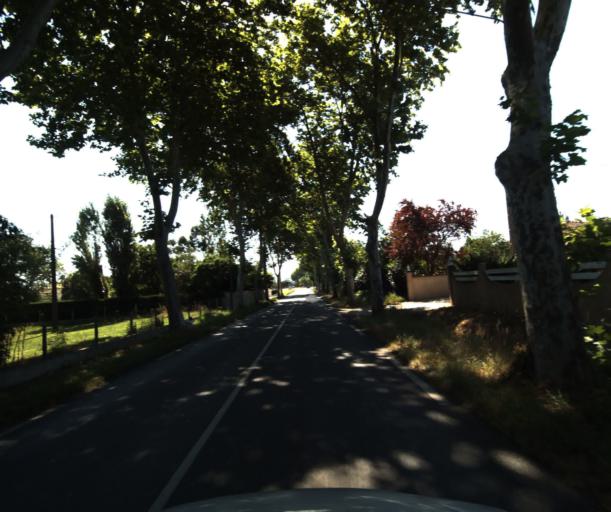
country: FR
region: Midi-Pyrenees
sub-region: Departement de la Haute-Garonne
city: Eaunes
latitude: 43.4213
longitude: 1.3718
